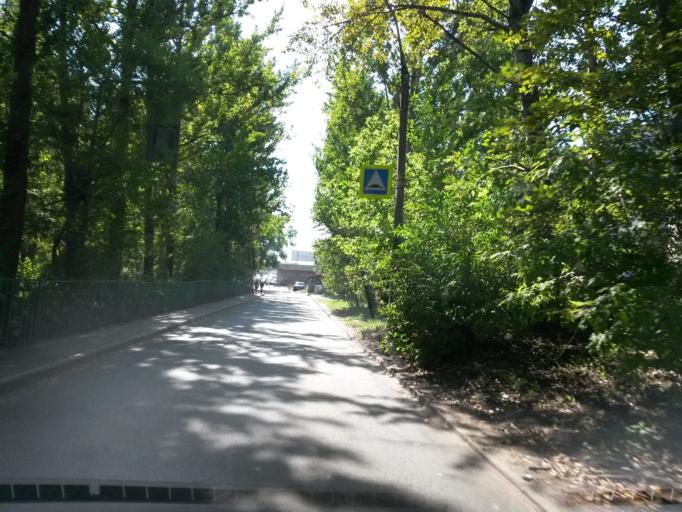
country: RU
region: Jaroslavl
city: Yaroslavl
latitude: 57.5752
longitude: 39.8518
